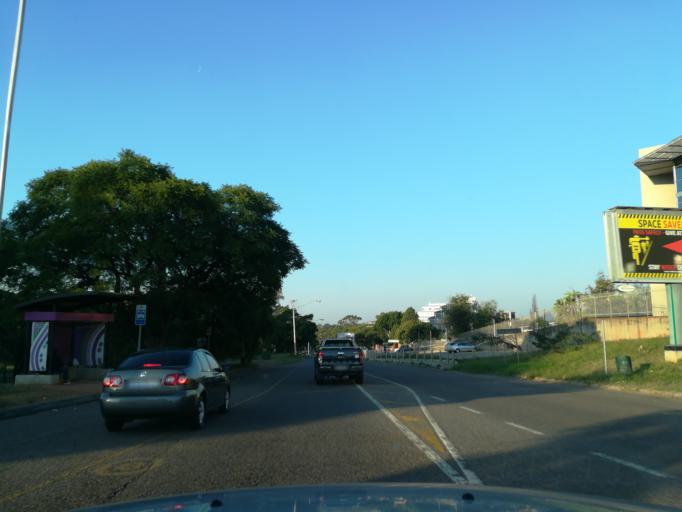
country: ZA
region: Gauteng
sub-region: City of Tshwane Metropolitan Municipality
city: Pretoria
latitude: -25.7704
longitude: 28.2150
